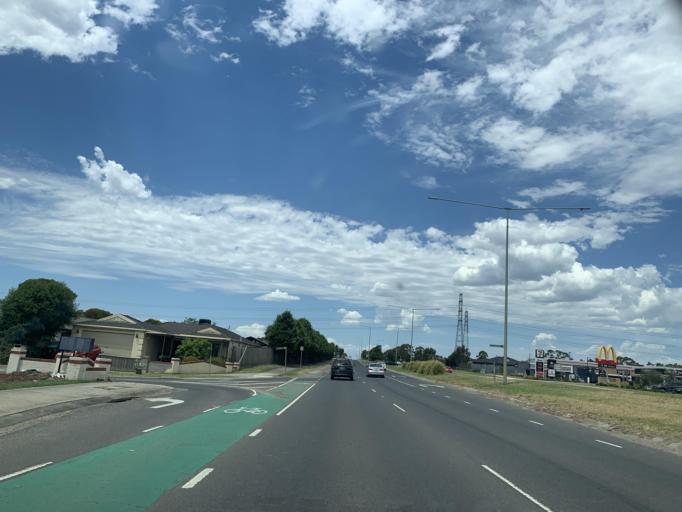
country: AU
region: Victoria
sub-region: Casey
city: Cranbourne West
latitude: -38.1100
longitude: 145.2588
